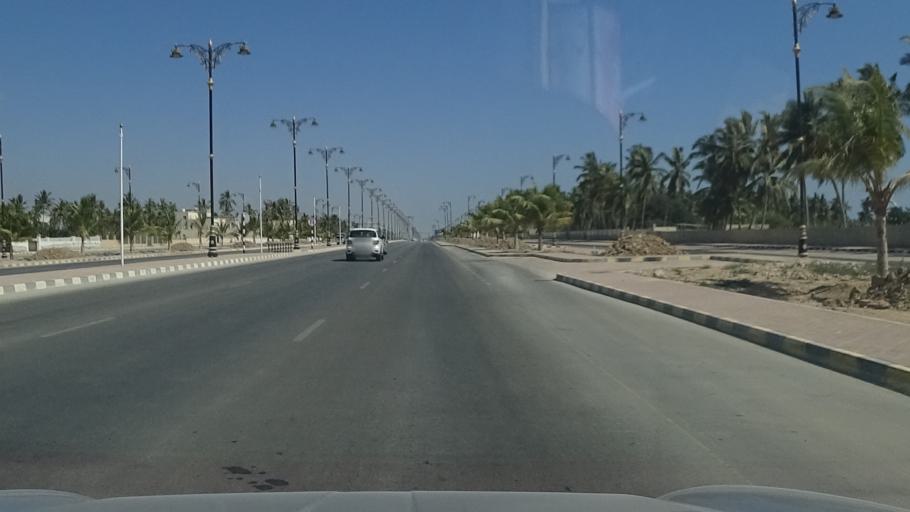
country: OM
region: Zufar
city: Salalah
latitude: 17.0360
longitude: 54.1537
